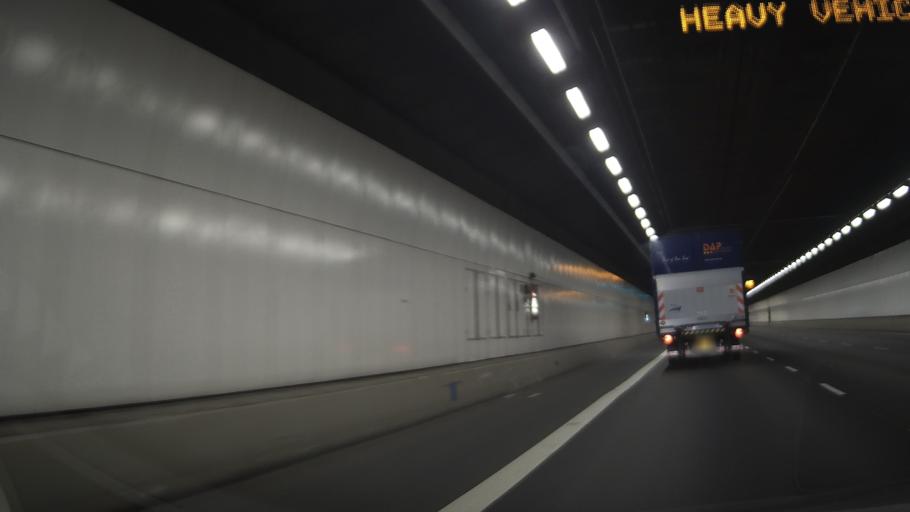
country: SG
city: Singapore
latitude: 1.3176
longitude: 103.8703
